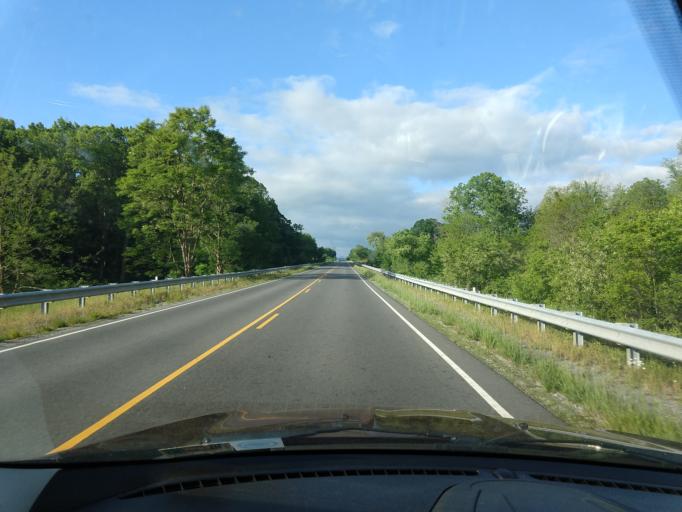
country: US
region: Virginia
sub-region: Wythe County
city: Wytheville
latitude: 36.8778
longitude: -80.9825
